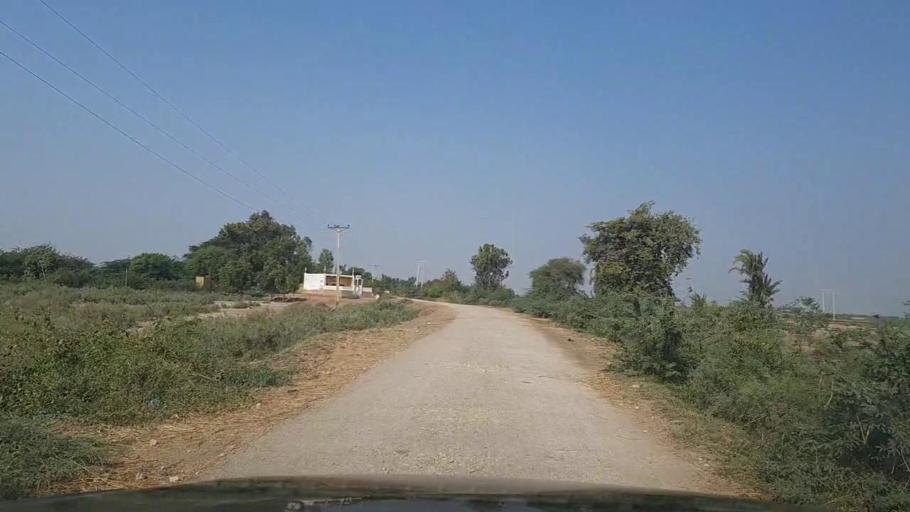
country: PK
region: Sindh
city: Thatta
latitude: 24.6115
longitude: 67.8230
